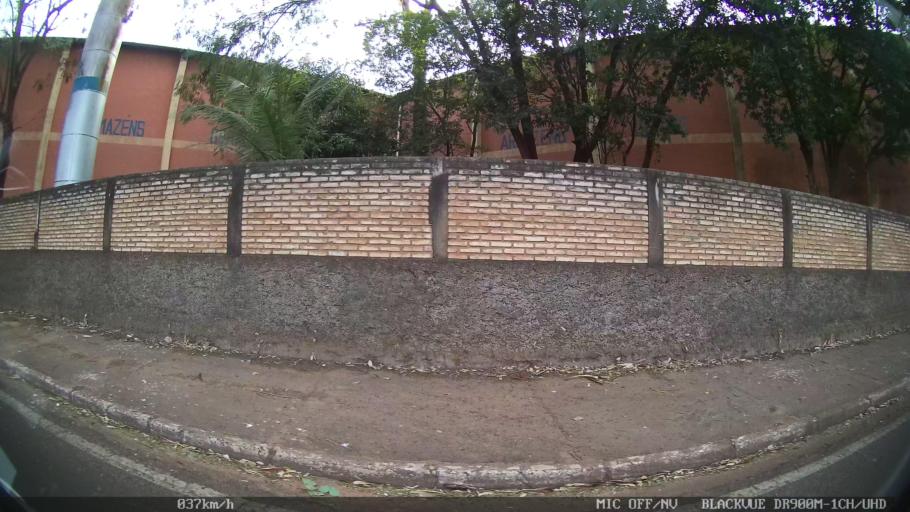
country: BR
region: Sao Paulo
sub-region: Catanduva
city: Catanduva
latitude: -21.1263
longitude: -48.9821
